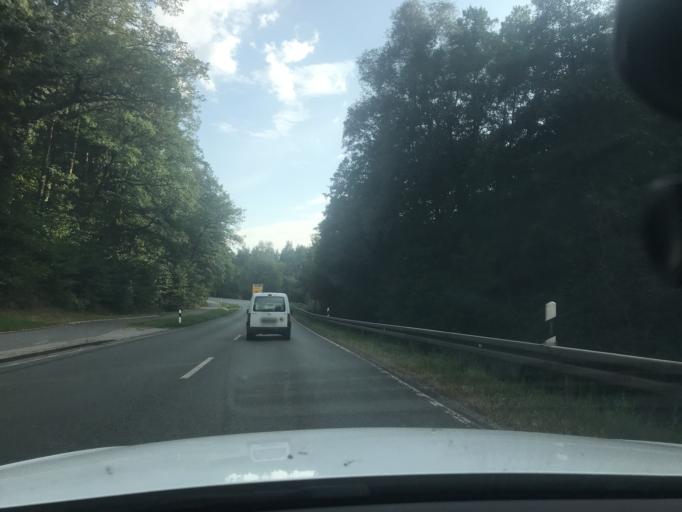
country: DE
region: Bavaria
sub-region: Upper Franconia
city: Creussen
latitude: 49.8402
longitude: 11.6205
